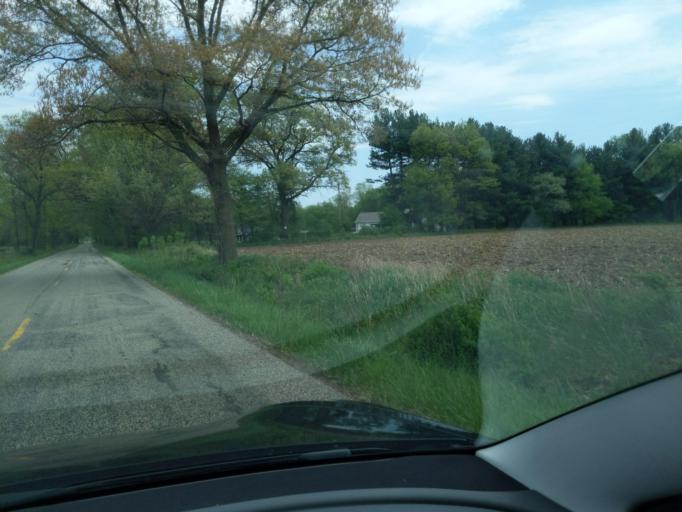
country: US
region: Michigan
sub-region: Ingham County
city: Leslie
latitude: 42.5041
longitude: -84.3524
